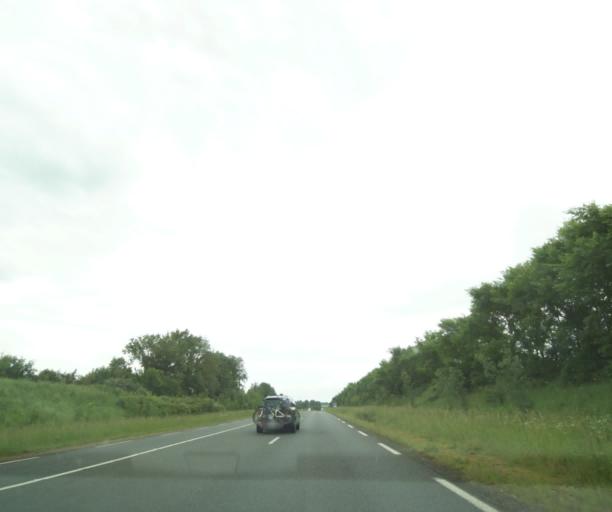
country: FR
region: Poitou-Charentes
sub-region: Departement des Deux-Sevres
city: Airvault
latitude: 46.8042
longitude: -0.2120
